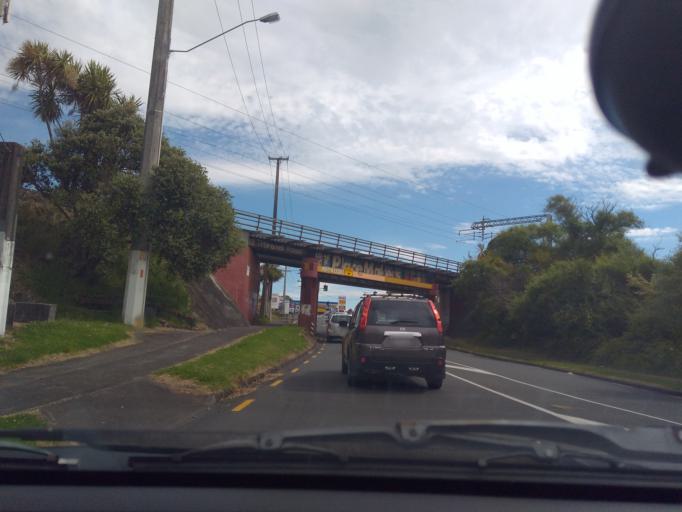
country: NZ
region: Auckland
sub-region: Auckland
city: Waitakere
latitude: -36.9108
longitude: 174.6762
